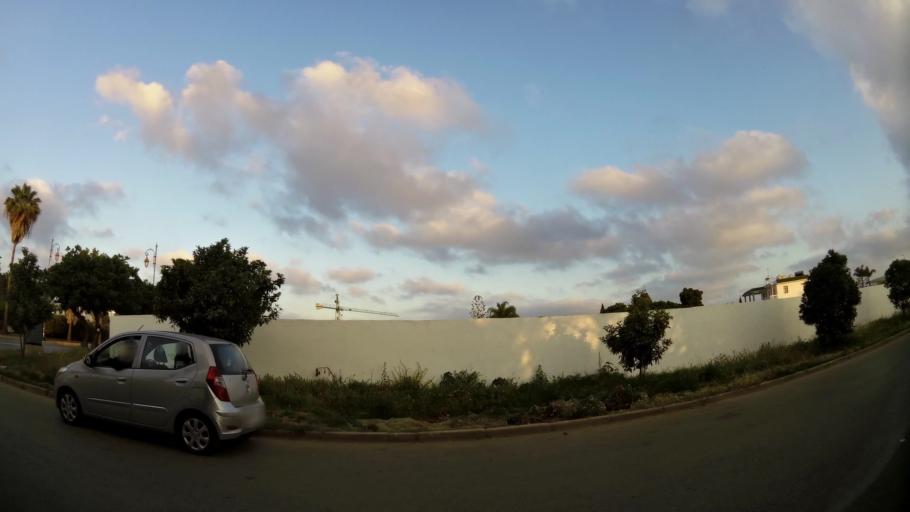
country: MA
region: Rabat-Sale-Zemmour-Zaer
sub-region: Rabat
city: Rabat
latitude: 33.9733
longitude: -6.8343
